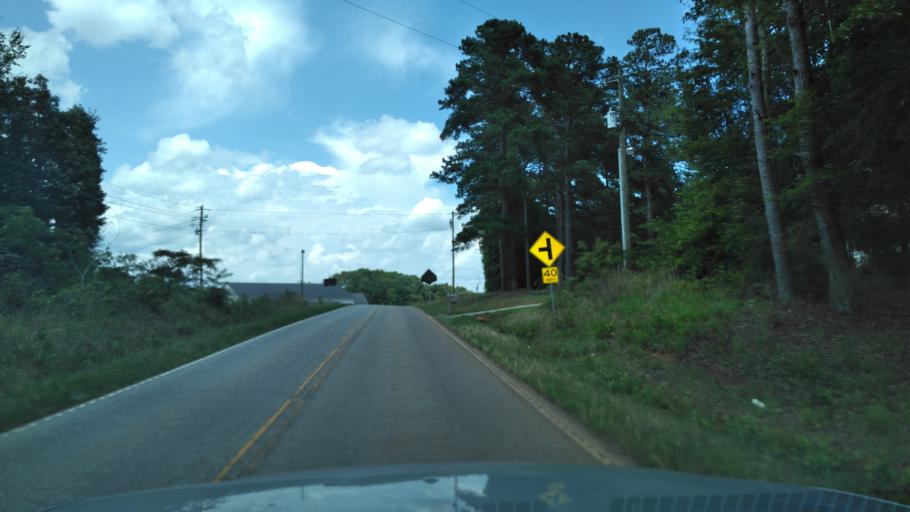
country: US
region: South Carolina
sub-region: Laurens County
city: Laurens
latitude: 34.4920
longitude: -82.1125
